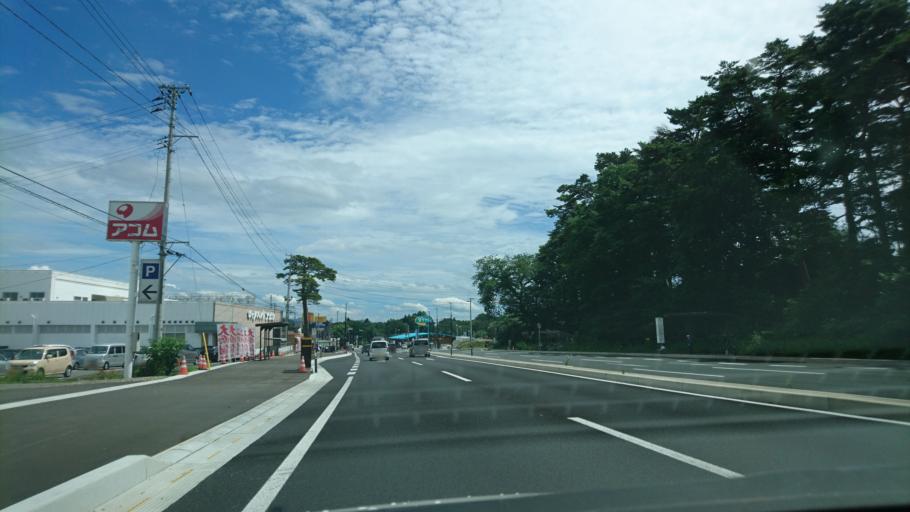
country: JP
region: Iwate
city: Morioka-shi
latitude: 39.7735
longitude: 141.1282
